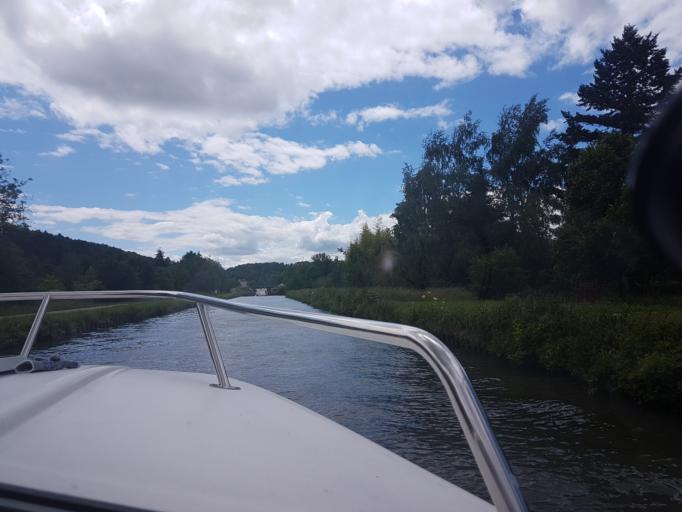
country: FR
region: Bourgogne
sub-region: Departement de l'Yonne
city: Vermenton
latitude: 47.6058
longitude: 3.6830
